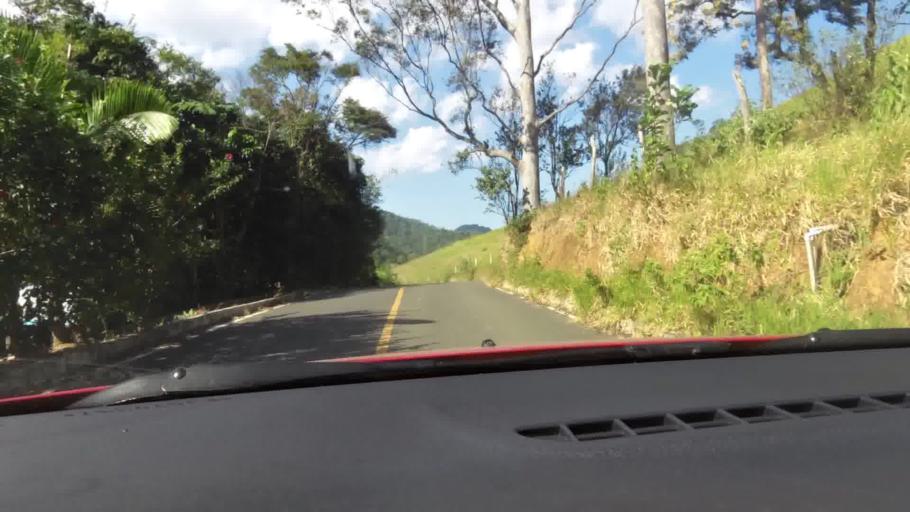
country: BR
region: Espirito Santo
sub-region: Guarapari
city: Guarapari
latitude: -20.5792
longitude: -40.5558
